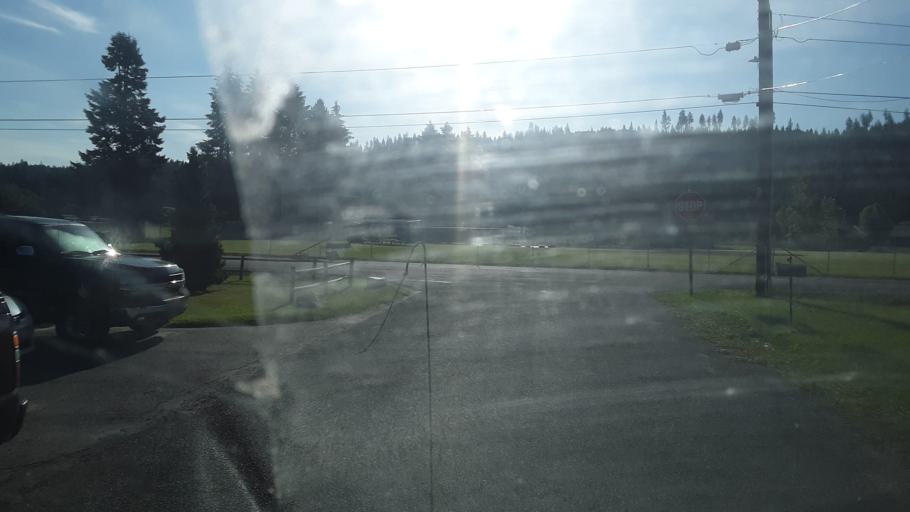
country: US
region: Idaho
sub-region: Boundary County
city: Bonners Ferry
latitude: 48.6782
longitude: -116.3279
